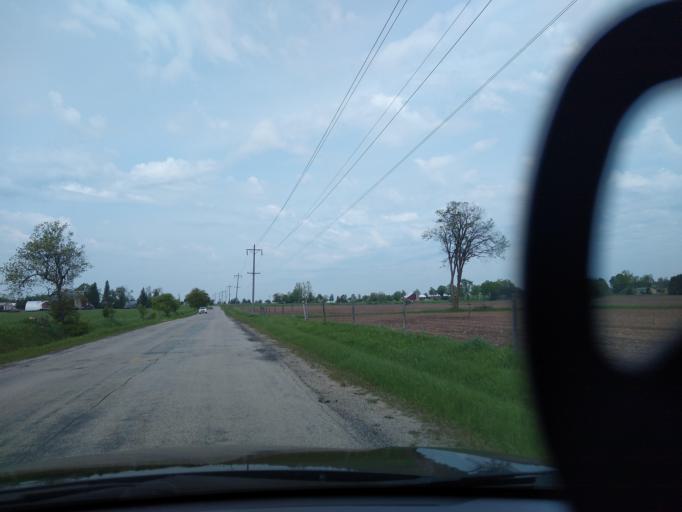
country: US
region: Michigan
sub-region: Delta County
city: Escanaba
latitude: 45.8216
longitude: -87.1416
